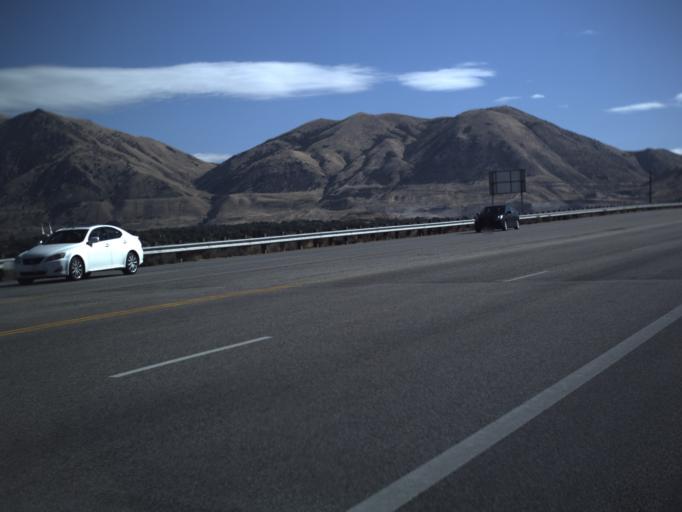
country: US
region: Utah
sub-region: Box Elder County
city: Perry
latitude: 41.4858
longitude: -112.0492
